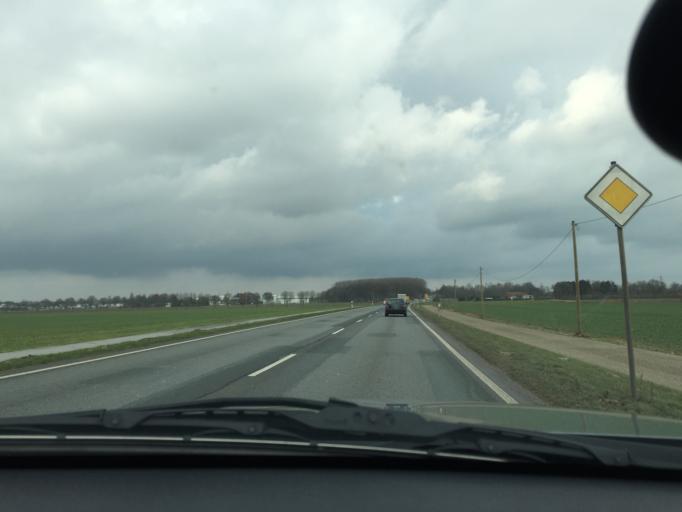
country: DE
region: North Rhine-Westphalia
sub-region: Regierungsbezirk Dusseldorf
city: Kleve
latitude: 51.7751
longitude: 6.1510
